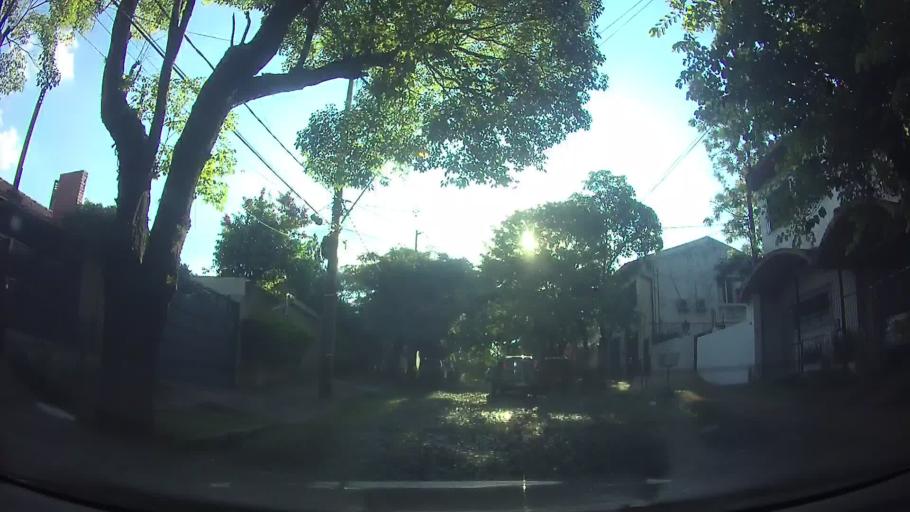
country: PY
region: Asuncion
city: Asuncion
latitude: -25.2800
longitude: -57.6009
